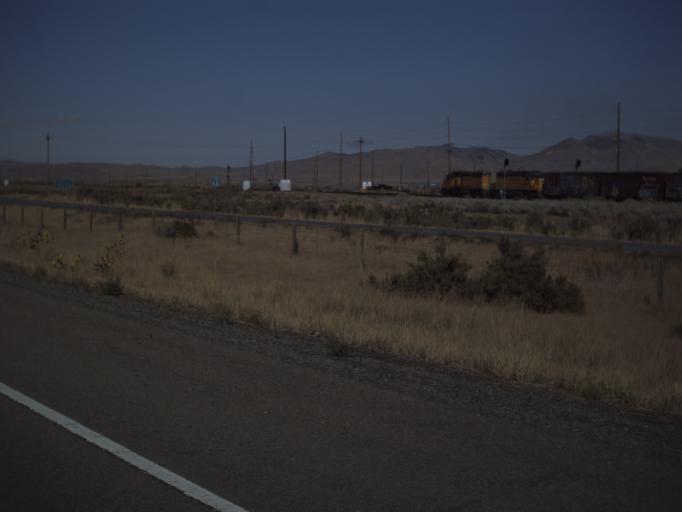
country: US
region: Utah
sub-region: Tooele County
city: Grantsville
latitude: 40.7466
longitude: -112.6555
